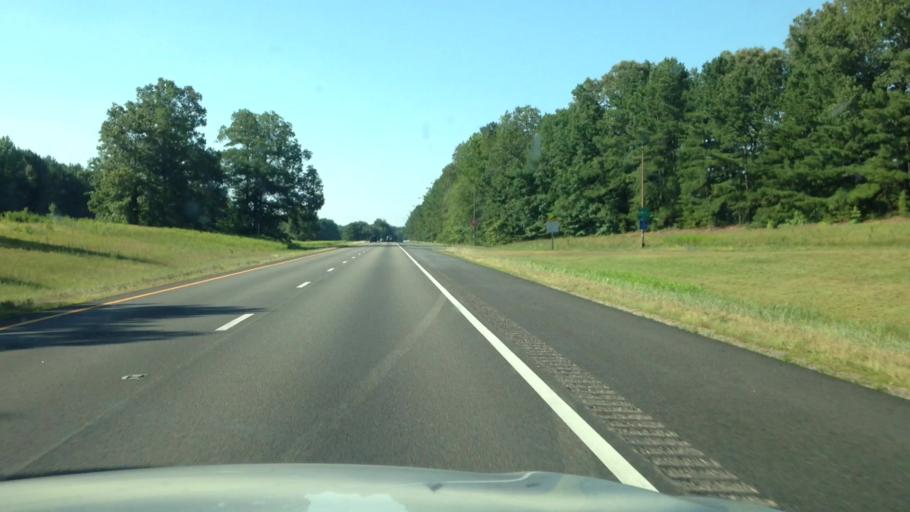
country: US
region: Virginia
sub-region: Sussex County
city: Sussex
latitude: 37.0181
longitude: -77.3917
